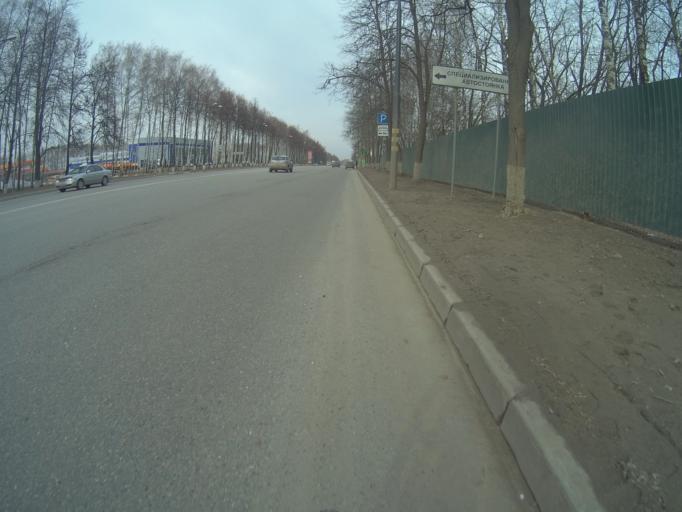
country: RU
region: Vladimir
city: Bogolyubovo
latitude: 56.1733
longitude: 40.4943
